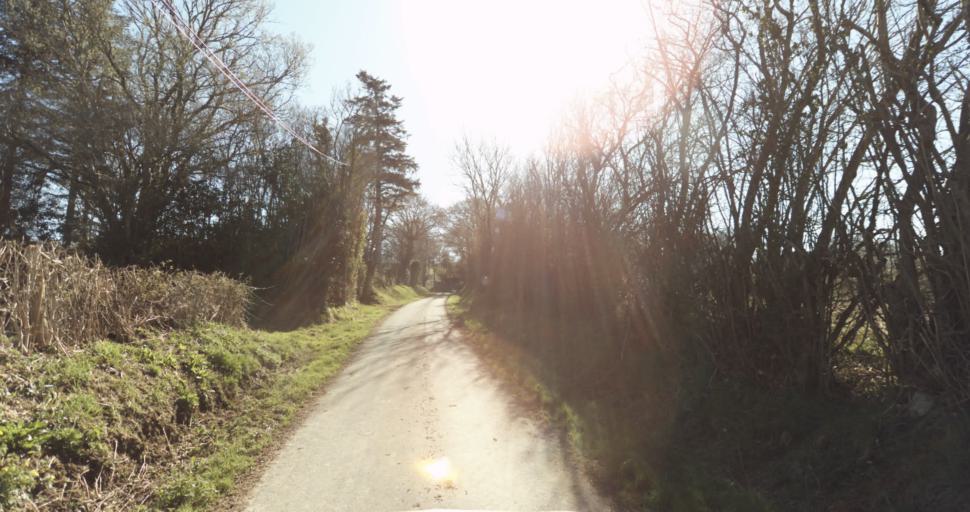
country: FR
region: Lower Normandy
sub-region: Departement de l'Orne
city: Trun
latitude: 48.9127
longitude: 0.0548
